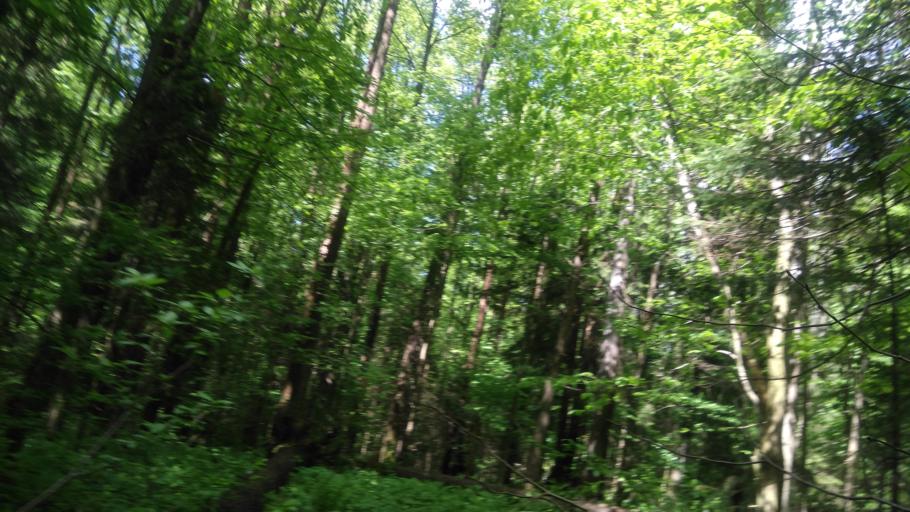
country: RU
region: Perm
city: Ferma
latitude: 57.9668
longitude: 56.3368
